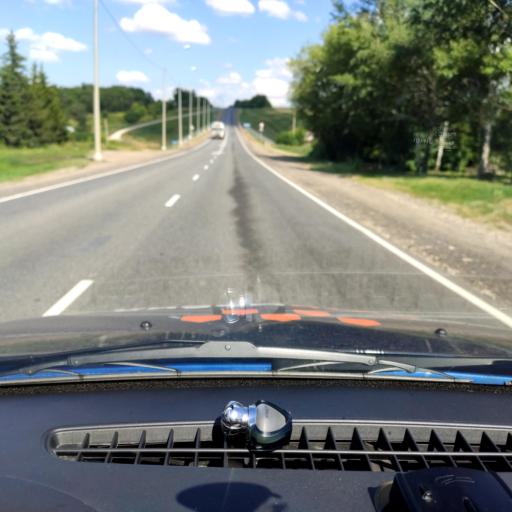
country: RU
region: Orjol
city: Livny
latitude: 52.4275
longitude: 37.7720
